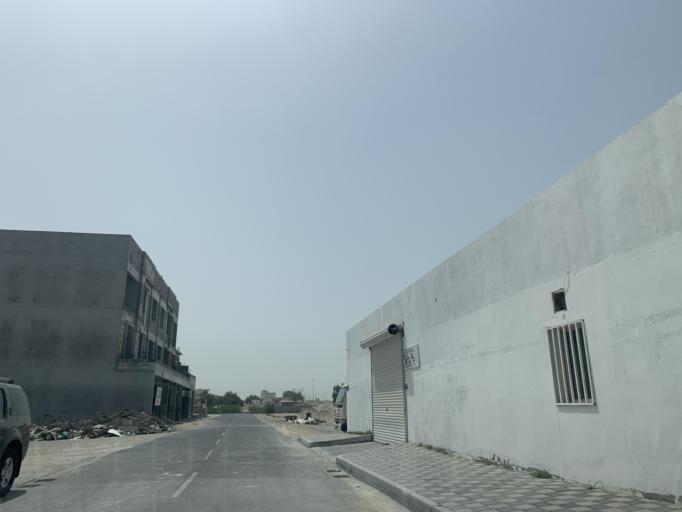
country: BH
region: Northern
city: Madinat `Isa
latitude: 26.1582
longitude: 50.5281
